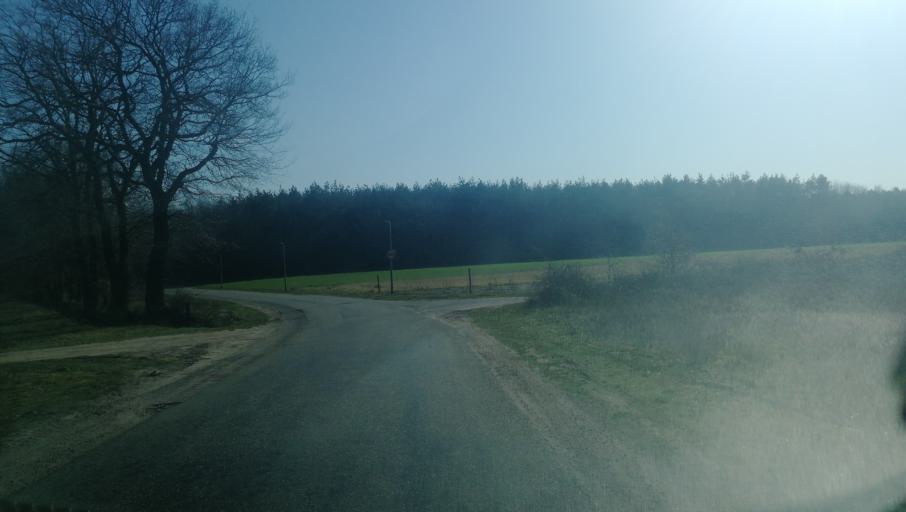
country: NL
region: Limburg
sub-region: Gemeente Venlo
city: Tegelen
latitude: 51.3855
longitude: 6.1026
